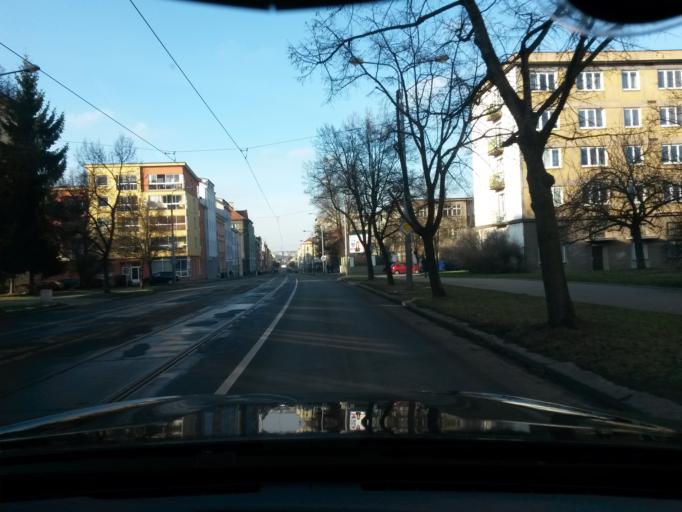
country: CZ
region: Plzensky
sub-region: Okres Plzen-Mesto
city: Pilsen
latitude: 49.7377
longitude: 13.3950
